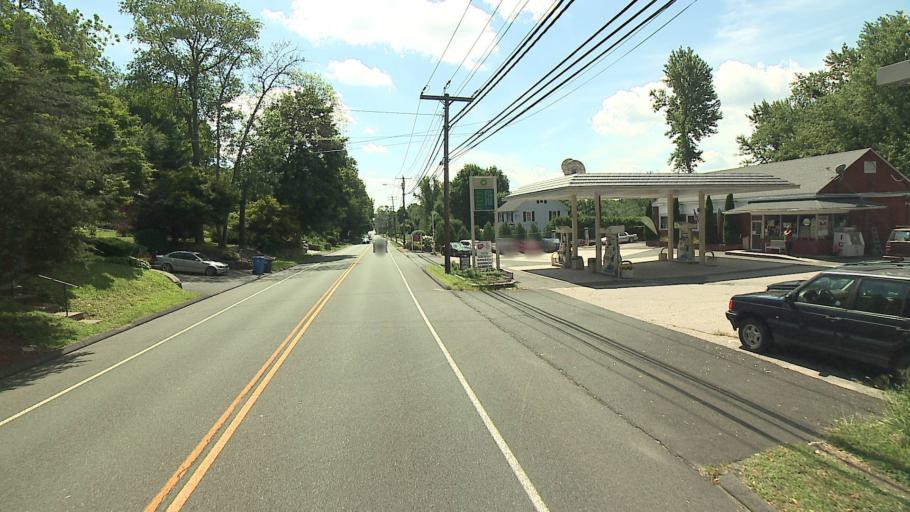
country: US
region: Connecticut
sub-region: Fairfield County
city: Trumbull
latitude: 41.2539
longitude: -73.2195
